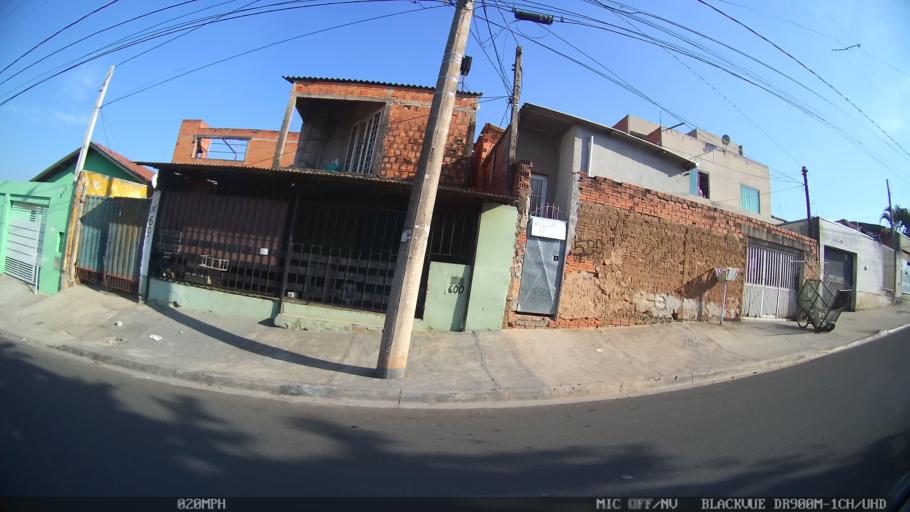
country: BR
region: Sao Paulo
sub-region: Campinas
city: Campinas
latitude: -22.9880
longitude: -47.1356
